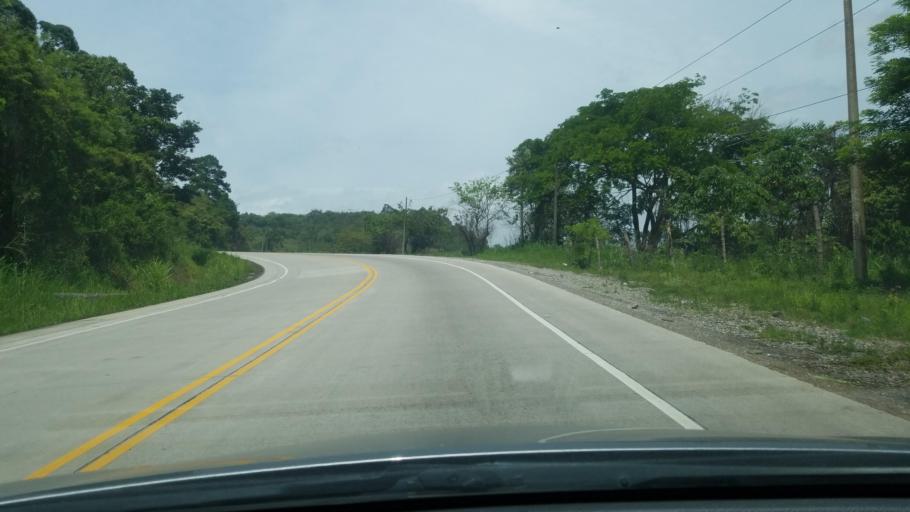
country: HN
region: Copan
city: Agua Caliente
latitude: 14.8630
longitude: -88.7889
